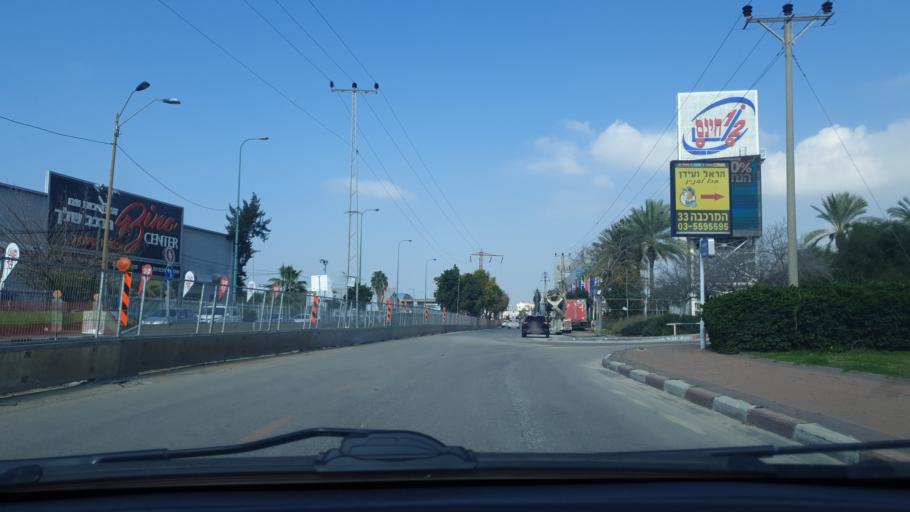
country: IL
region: Tel Aviv
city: Azor
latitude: 32.0082
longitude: 34.8079
